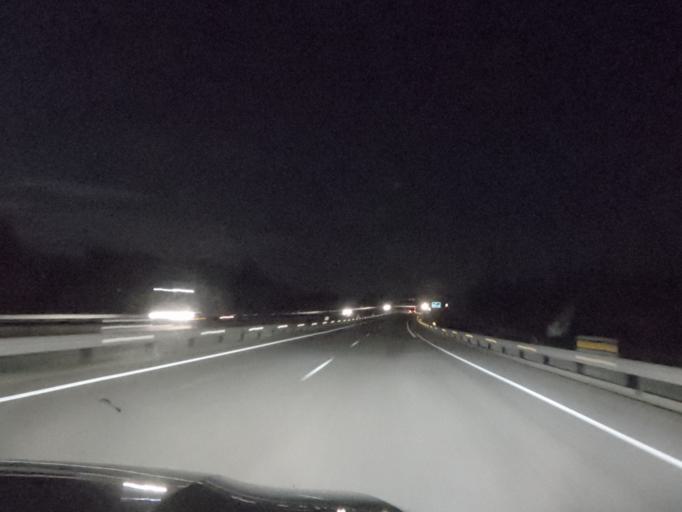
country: ES
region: Galicia
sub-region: Provincia de Ourense
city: Ambia
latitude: 42.1488
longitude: -7.7522
